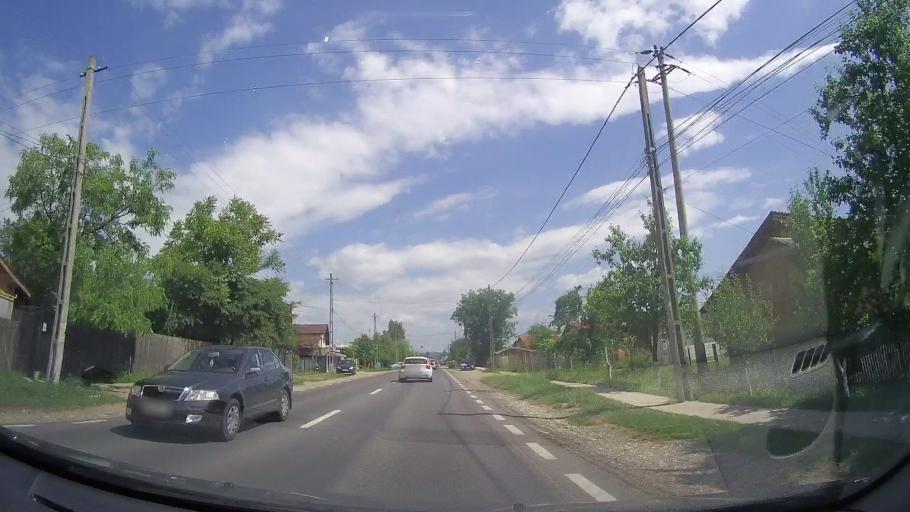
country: RO
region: Prahova
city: Valenii de Munte
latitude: 45.1691
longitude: 26.0326
